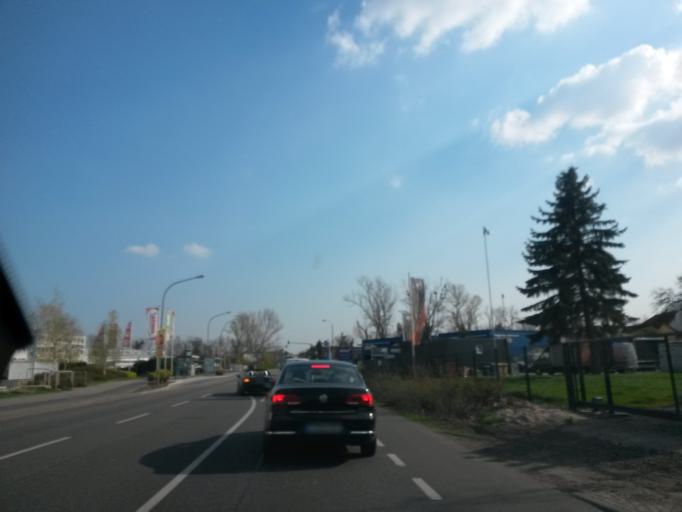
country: DE
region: Berlin
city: Wannsee
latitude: 52.3696
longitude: 13.1284
